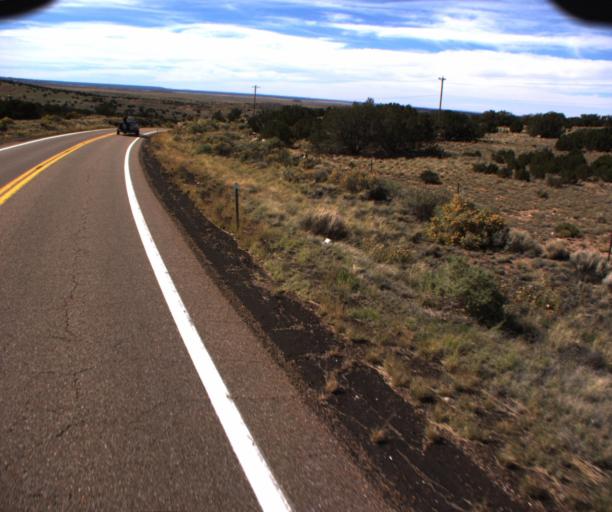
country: US
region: Arizona
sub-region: Apache County
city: Saint Johns
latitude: 34.4827
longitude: -109.5687
